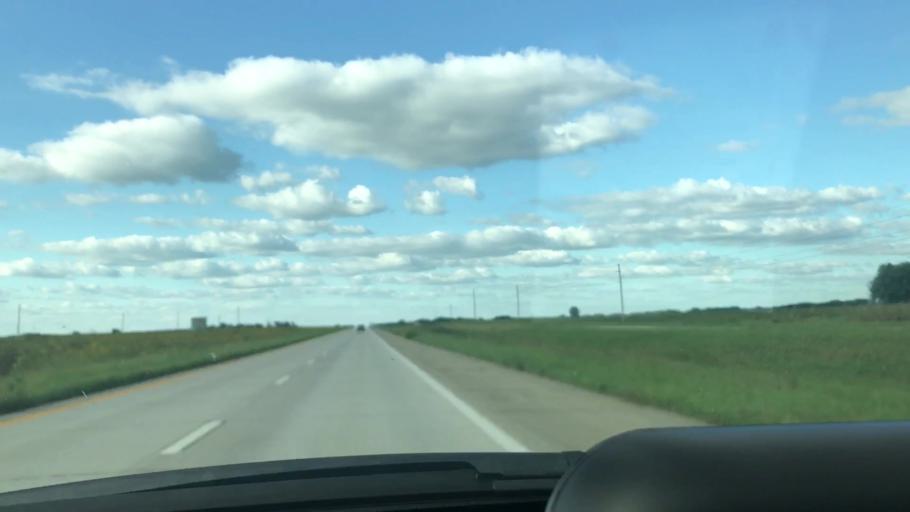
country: US
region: Missouri
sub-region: Benton County
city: Cole Camp
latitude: 38.5122
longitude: -93.2726
